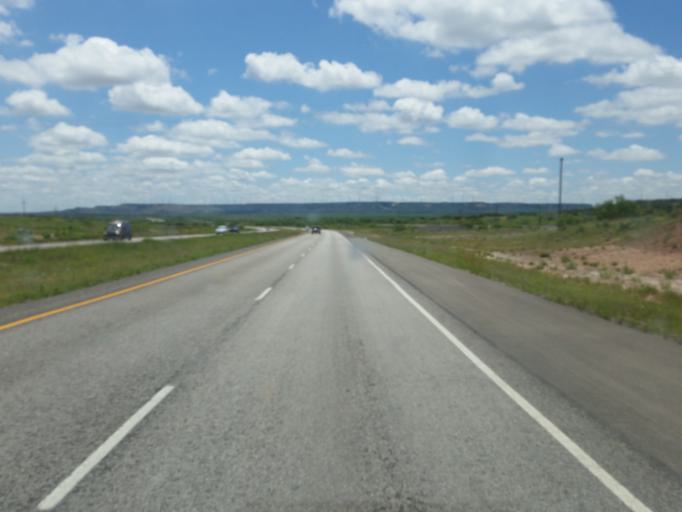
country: US
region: Texas
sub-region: Garza County
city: Post
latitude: 33.0179
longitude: -101.1791
